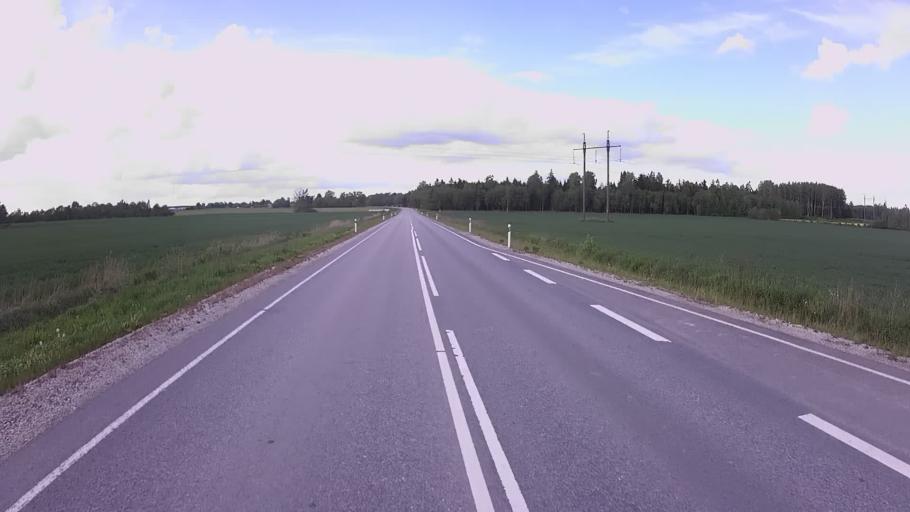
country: EE
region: Jogevamaa
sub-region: Mustvee linn
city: Mustvee
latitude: 58.8907
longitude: 26.8122
